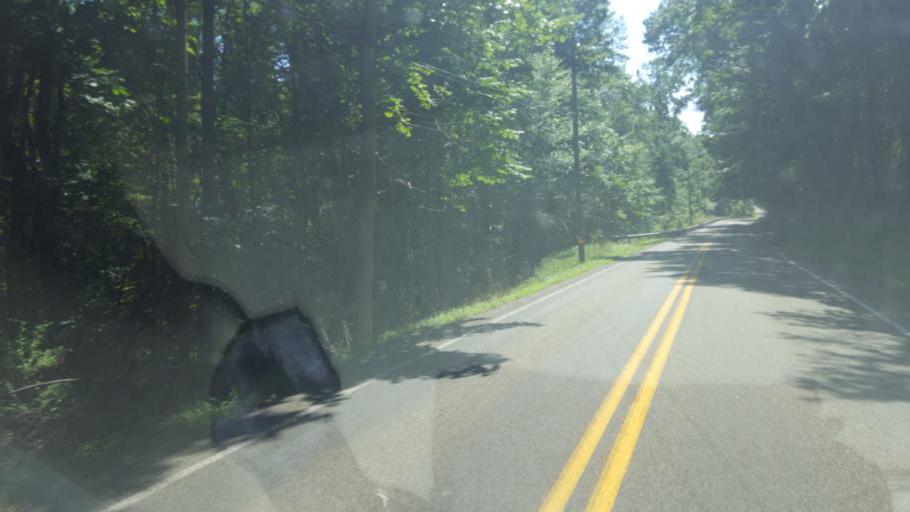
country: US
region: Pennsylvania
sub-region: Clarion County
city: Knox
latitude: 41.1562
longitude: -79.6824
